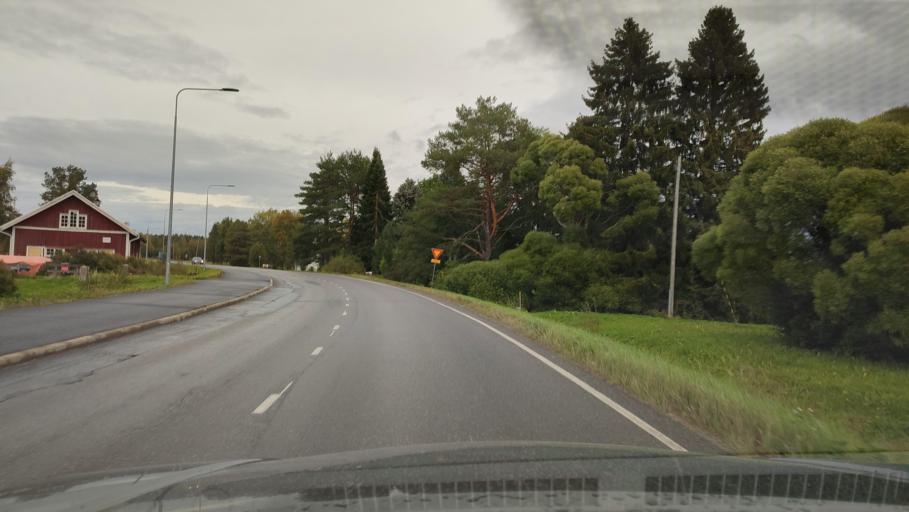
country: FI
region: Ostrobothnia
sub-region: Sydosterbotten
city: Kristinestad
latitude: 62.2586
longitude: 21.5296
